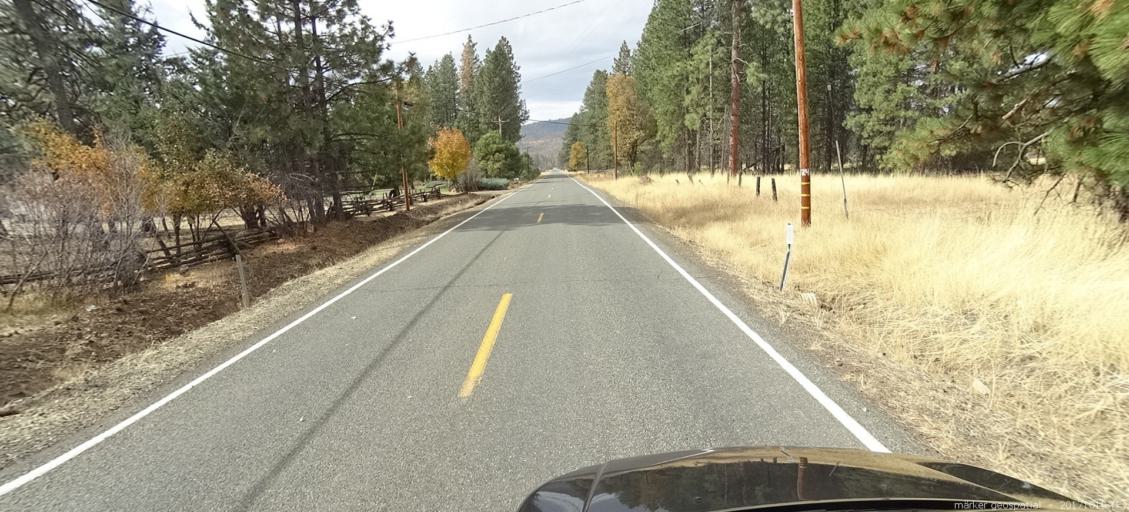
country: US
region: California
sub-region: Shasta County
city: Burney
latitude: 41.0616
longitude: -121.5178
